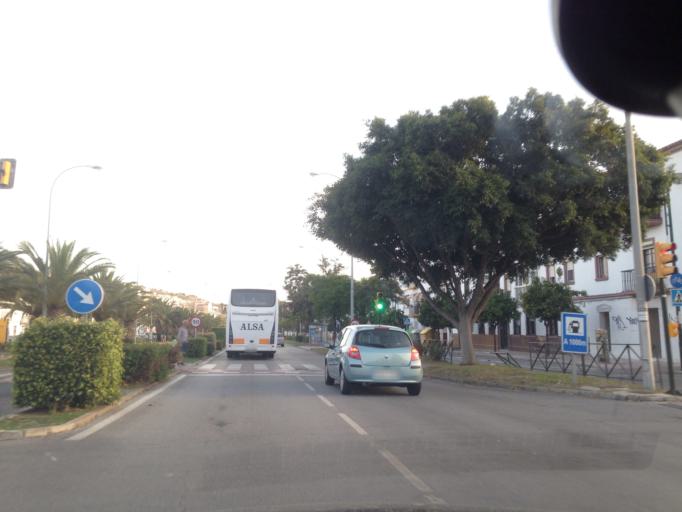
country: ES
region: Andalusia
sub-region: Provincia de Malaga
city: Malaga
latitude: 36.7497
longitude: -4.4242
